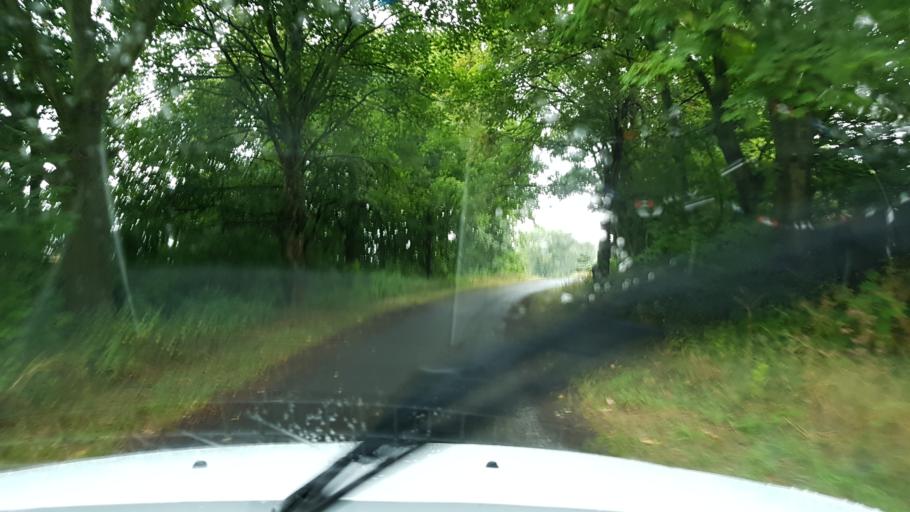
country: PL
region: West Pomeranian Voivodeship
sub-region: Powiat mysliborski
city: Barlinek
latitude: 52.9911
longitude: 15.1218
